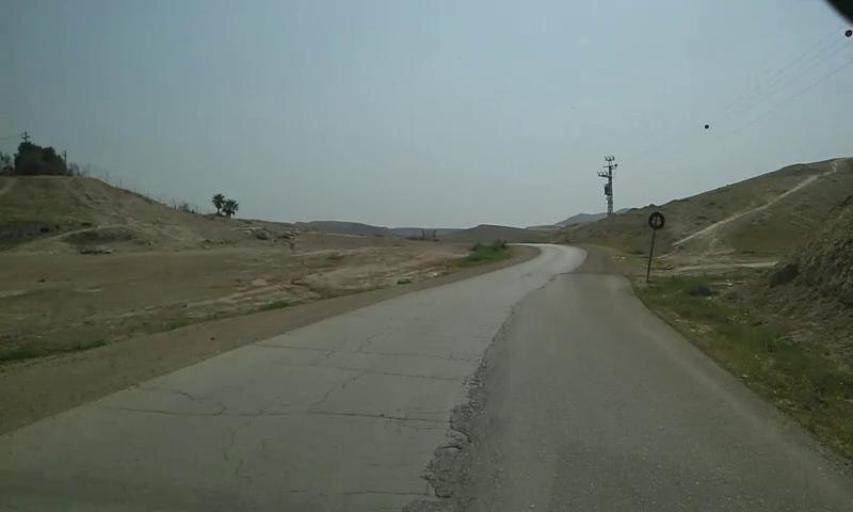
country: PS
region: West Bank
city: Jericho
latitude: 31.7871
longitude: 35.4304
